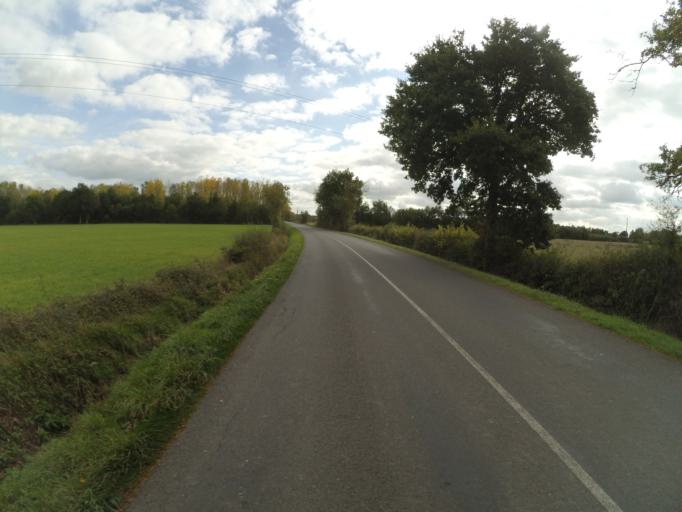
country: FR
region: Pays de la Loire
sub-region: Departement de la Loire-Atlantique
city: Bouvron
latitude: 47.4640
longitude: -1.8353
